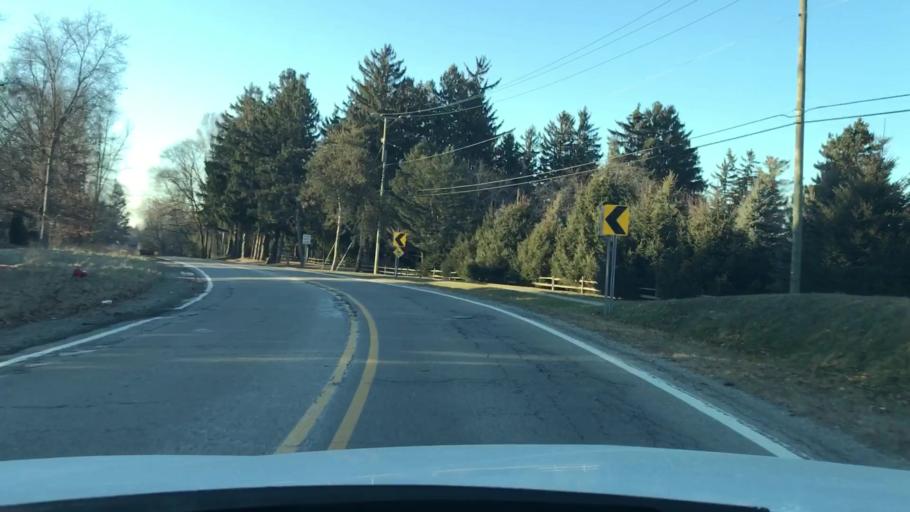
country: US
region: Michigan
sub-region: Oakland County
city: West Bloomfield Township
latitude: 42.5962
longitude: -83.4028
